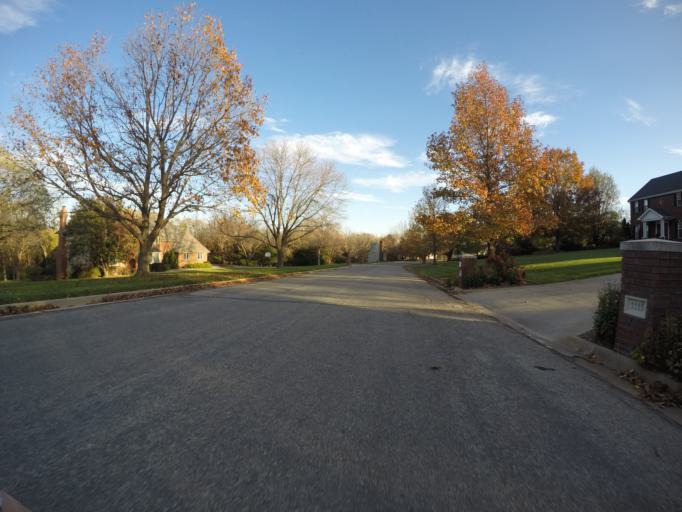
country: US
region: Kansas
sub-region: Riley County
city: Manhattan
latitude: 39.1908
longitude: -96.6308
